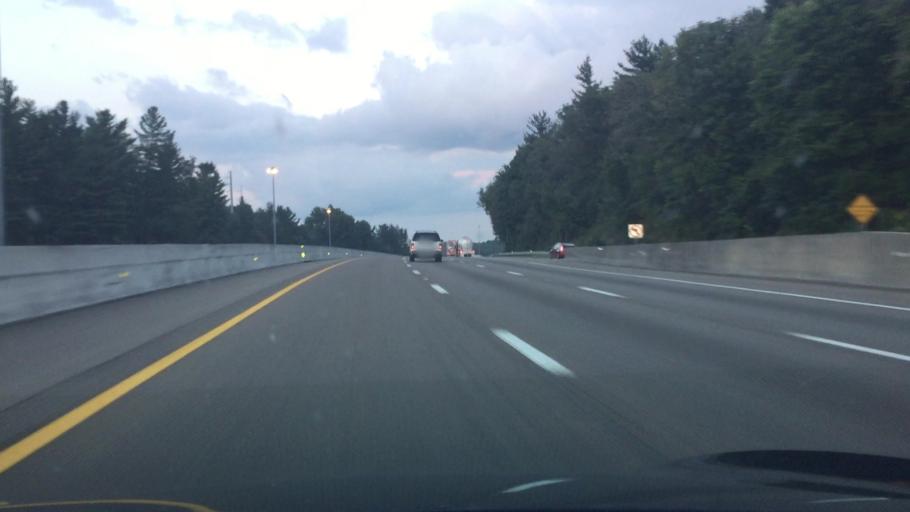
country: US
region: Virginia
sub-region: City of Bristol
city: Bristol
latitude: 36.6254
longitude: -82.1782
